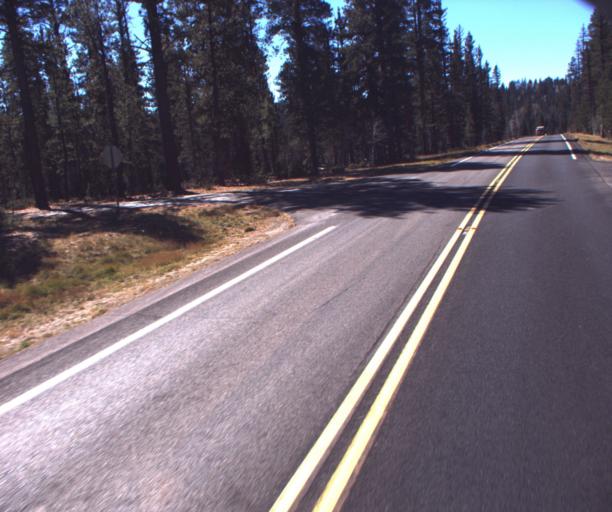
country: US
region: Arizona
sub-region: Coconino County
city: Grand Canyon
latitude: 36.4545
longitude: -112.1322
